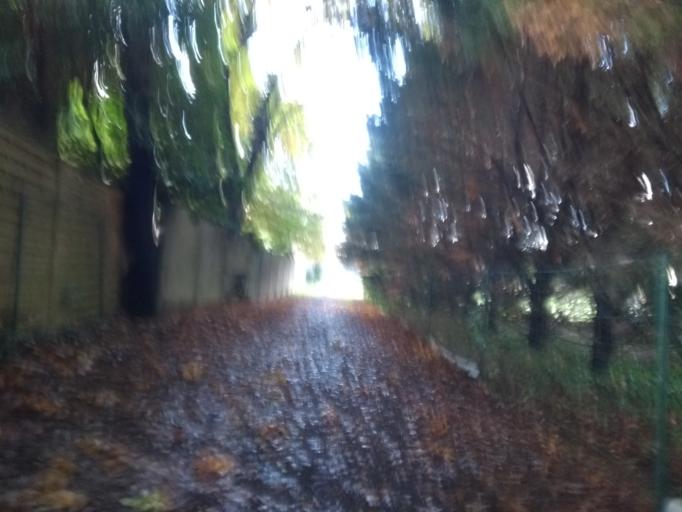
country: FR
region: Aquitaine
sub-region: Departement de la Gironde
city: Canejan
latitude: 44.7656
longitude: -0.6518
